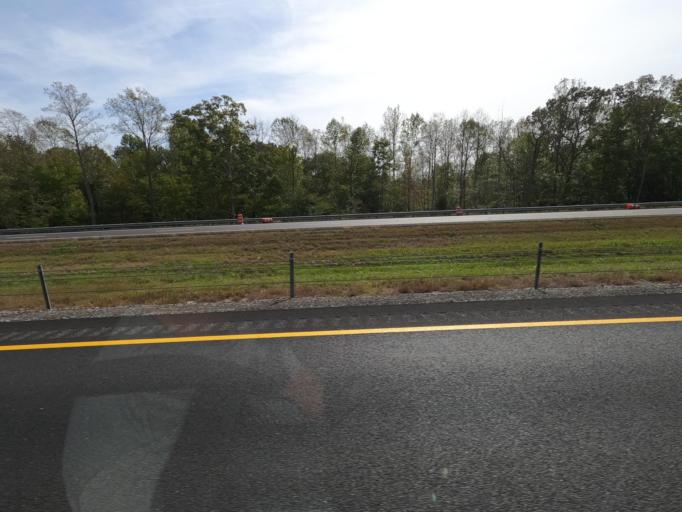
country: US
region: Tennessee
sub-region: Decatur County
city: Parsons
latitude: 35.8344
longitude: -88.0976
